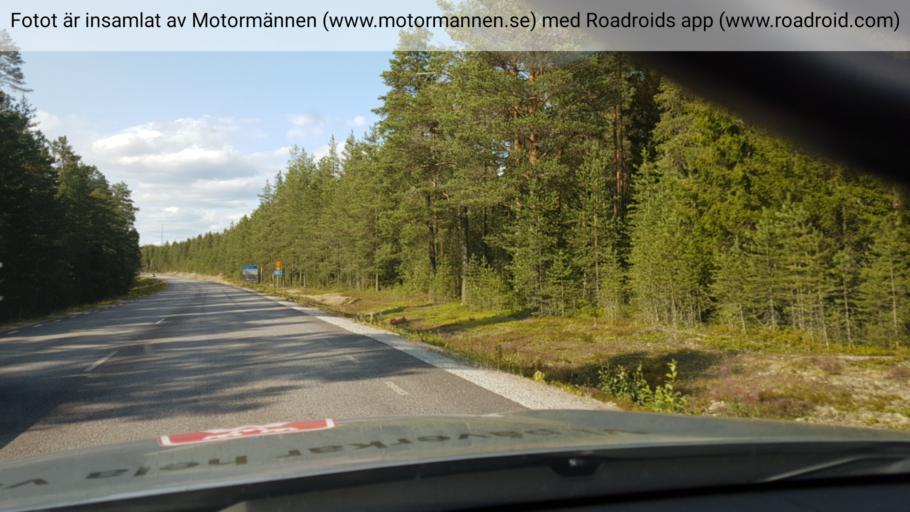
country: SE
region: Norrbotten
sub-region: Pitea Kommun
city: Pitea
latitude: 65.2656
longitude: 21.5358
